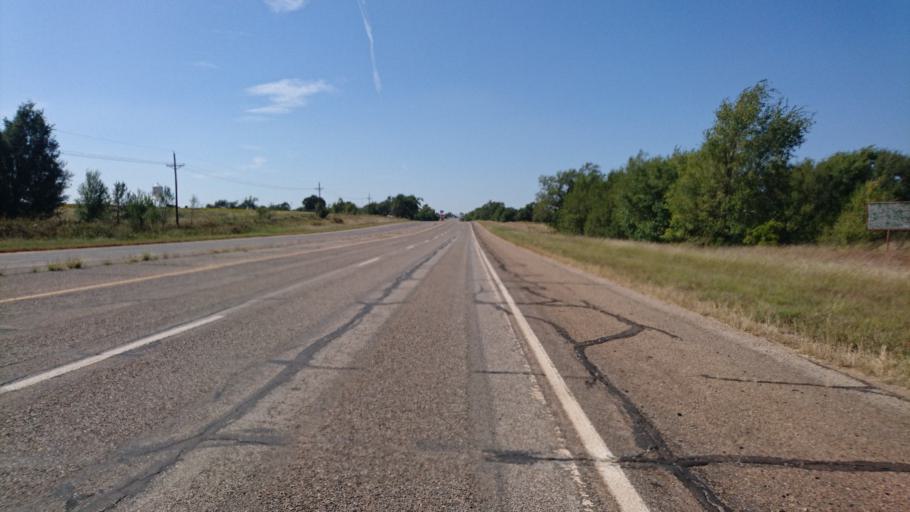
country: US
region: Texas
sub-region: Wheeler County
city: Shamrock
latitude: 35.2267
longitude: -100.2298
